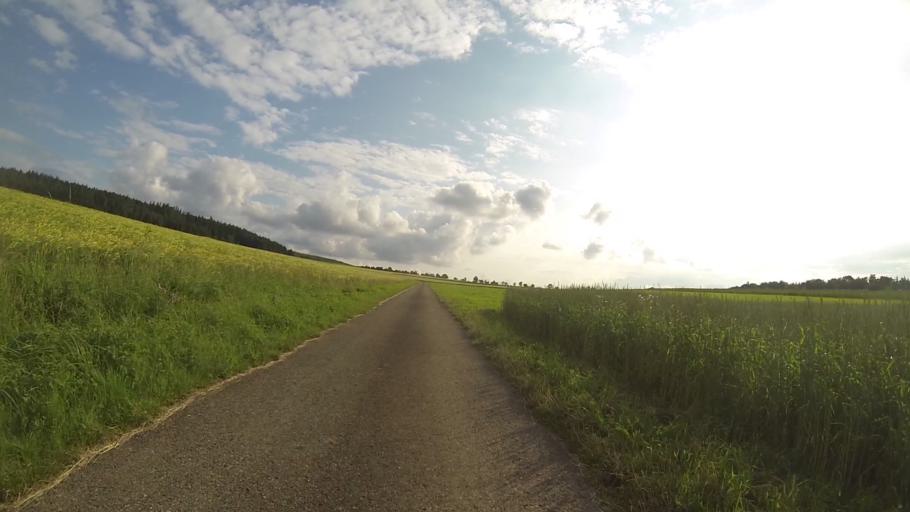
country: DE
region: Baden-Wuerttemberg
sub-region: Regierungsbezirk Stuttgart
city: Neresheim
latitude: 48.7377
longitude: 10.2823
